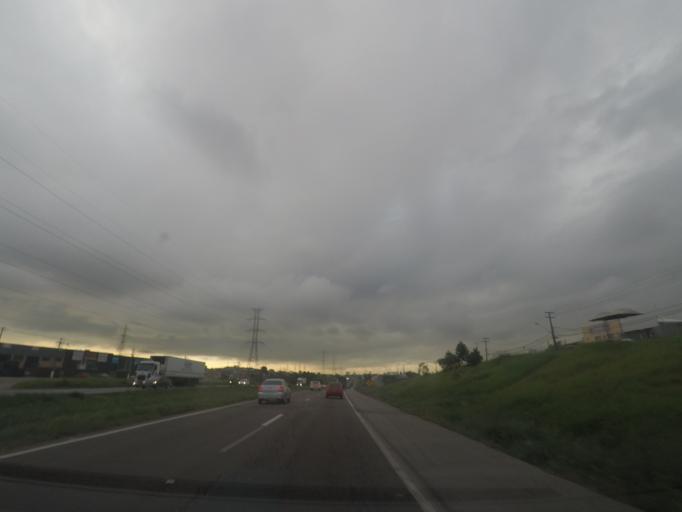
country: BR
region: Parana
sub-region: Curitiba
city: Curitiba
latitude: -25.5062
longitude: -49.3405
